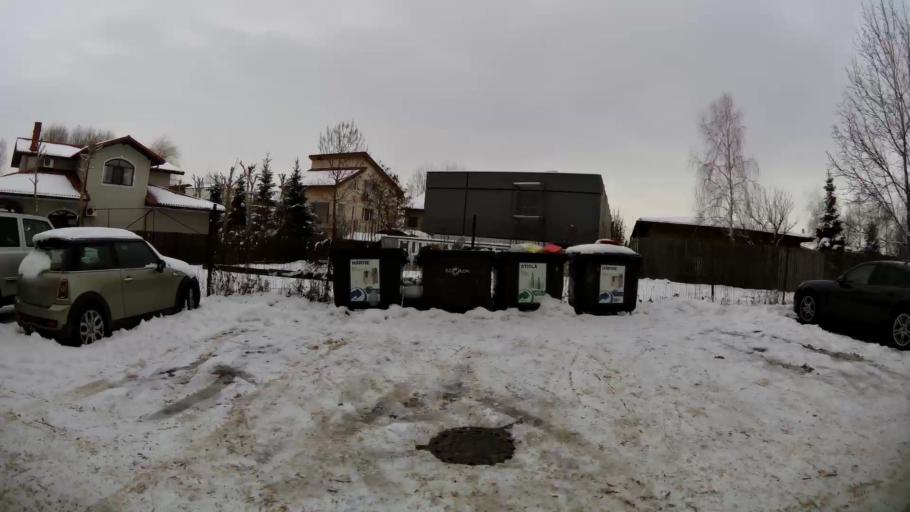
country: RO
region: Ilfov
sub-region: Comuna Otopeni
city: Otopeni
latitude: 44.5119
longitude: 26.1033
